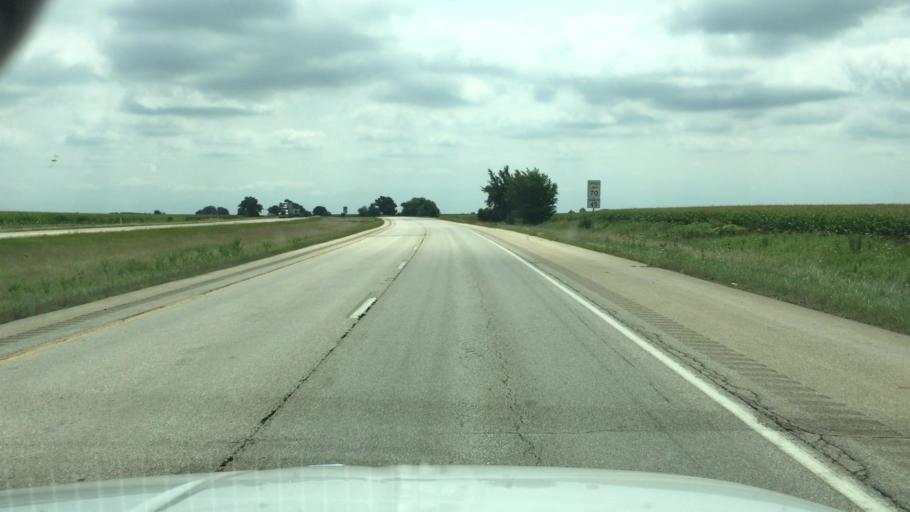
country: US
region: Illinois
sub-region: Knox County
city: Knoxville
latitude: 40.9068
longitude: -90.2410
